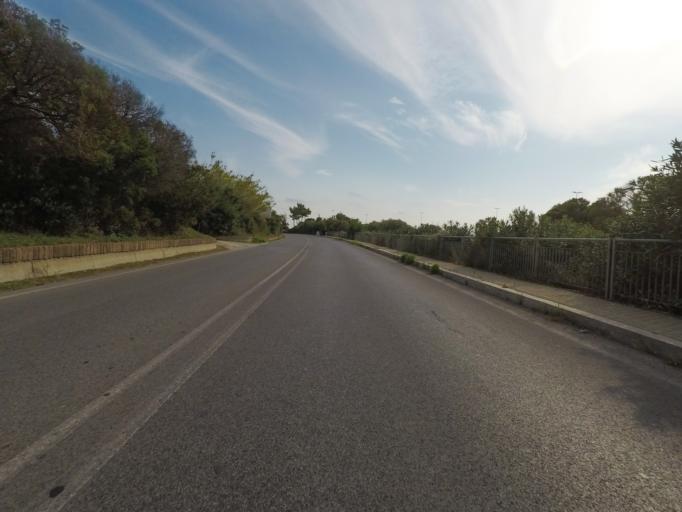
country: IT
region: Latium
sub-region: Citta metropolitana di Roma Capitale
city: Civitavecchia
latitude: 42.0649
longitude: 11.8139
